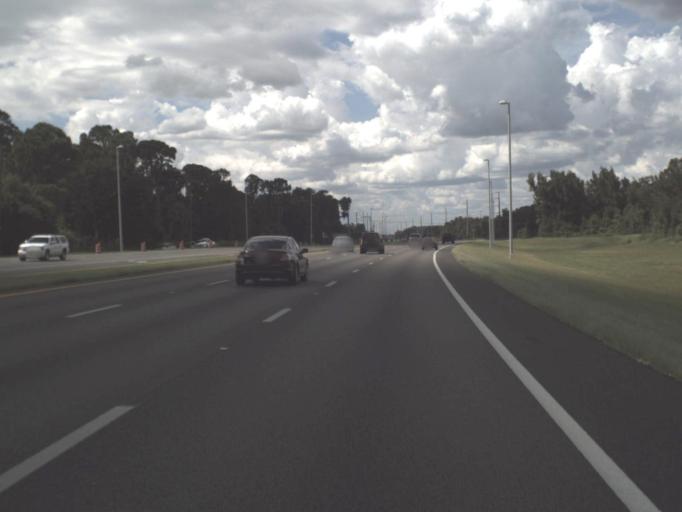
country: US
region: Florida
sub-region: Polk County
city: Bartow
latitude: 27.9263
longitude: -81.8526
